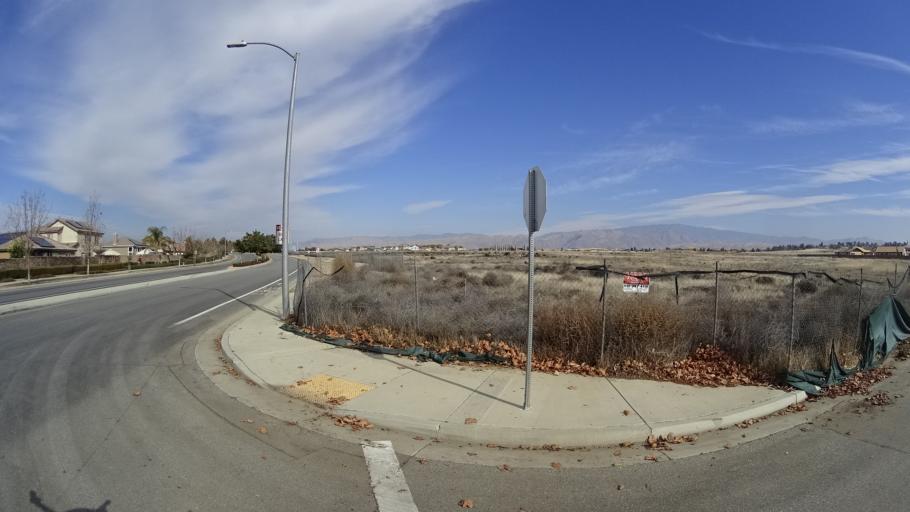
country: US
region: California
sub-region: Kern County
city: Oildale
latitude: 35.4037
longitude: -118.8875
